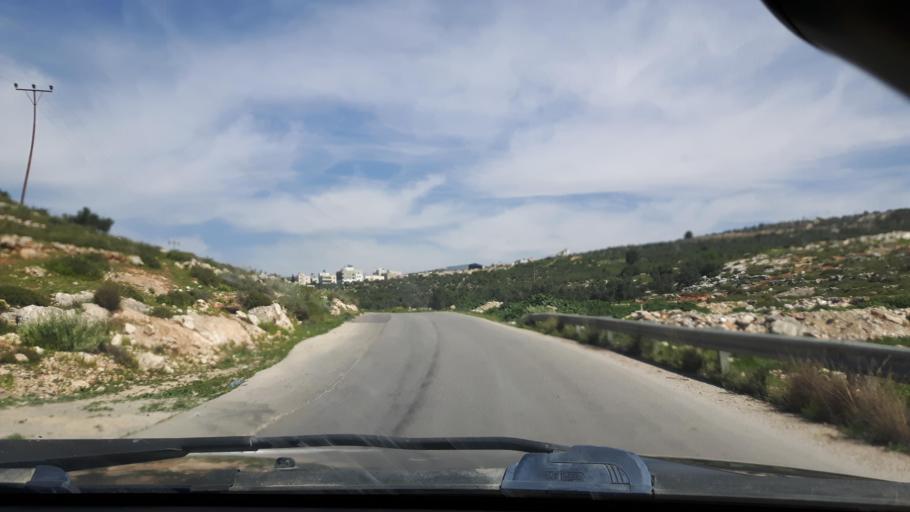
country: PS
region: West Bank
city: Bayt `Ur at Tahta
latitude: 31.8889
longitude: 35.0858
